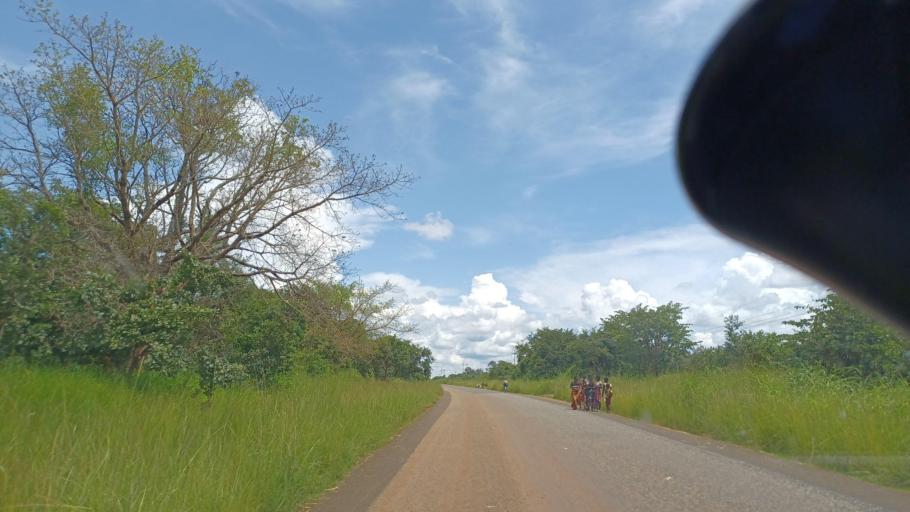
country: ZM
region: North-Western
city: Solwezi
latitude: -12.5593
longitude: 26.1424
